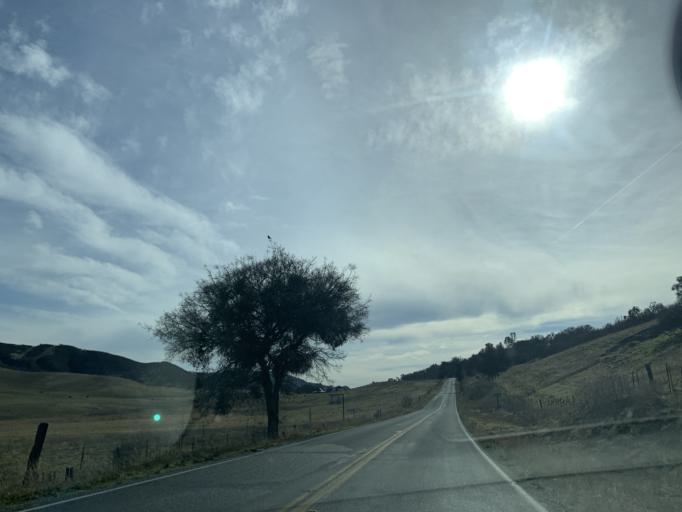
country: US
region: California
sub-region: Monterey County
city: Greenfield
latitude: 36.5014
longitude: -121.0865
